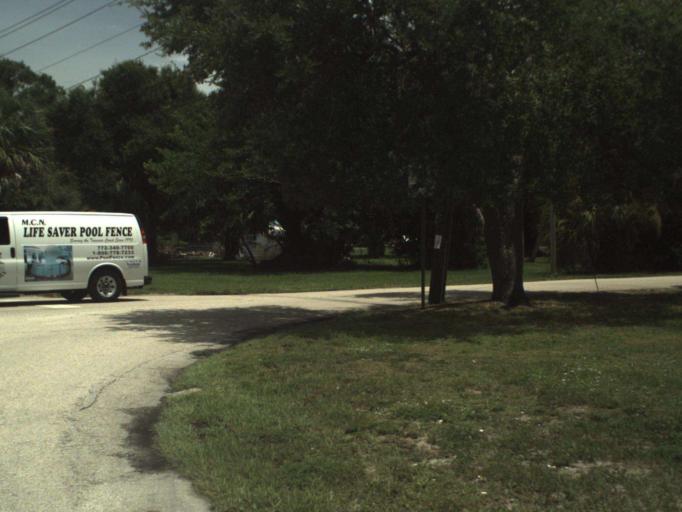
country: US
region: Florida
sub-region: Saint Lucie County
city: White City
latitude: 27.3743
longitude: -80.3385
